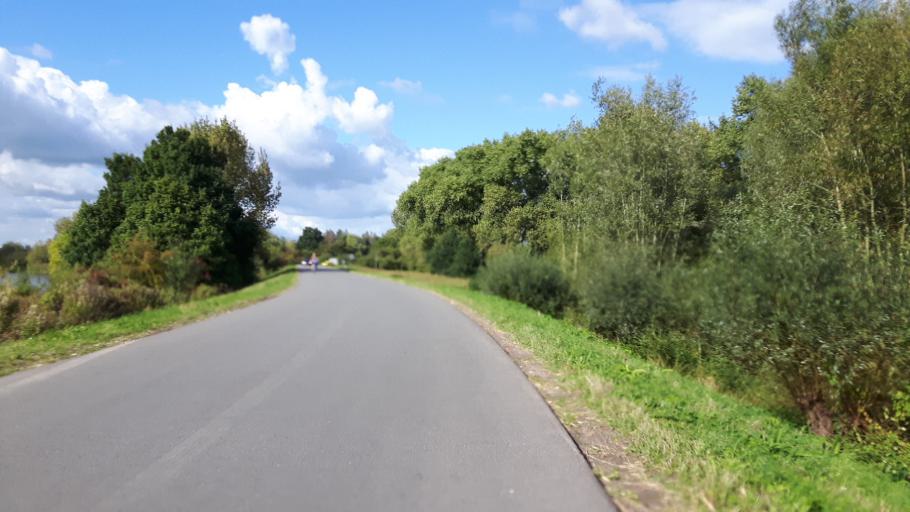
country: NL
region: South Holland
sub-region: Gemeente Leerdam
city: Leerdam
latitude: 51.8616
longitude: 5.0642
